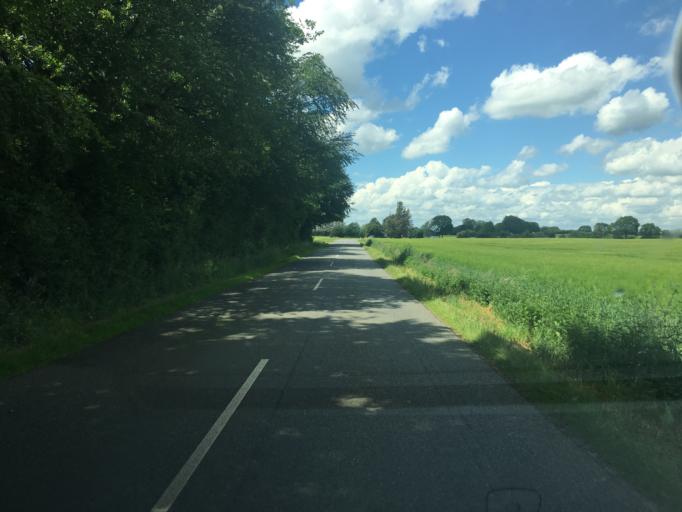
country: DK
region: South Denmark
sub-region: Haderslev Kommune
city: Vojens
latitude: 55.2788
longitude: 9.3225
